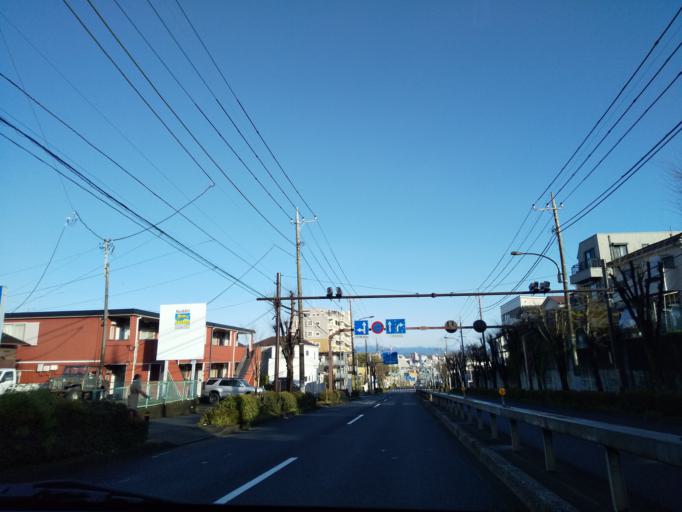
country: JP
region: Tokyo
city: Hachioji
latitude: 35.6376
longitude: 139.3609
